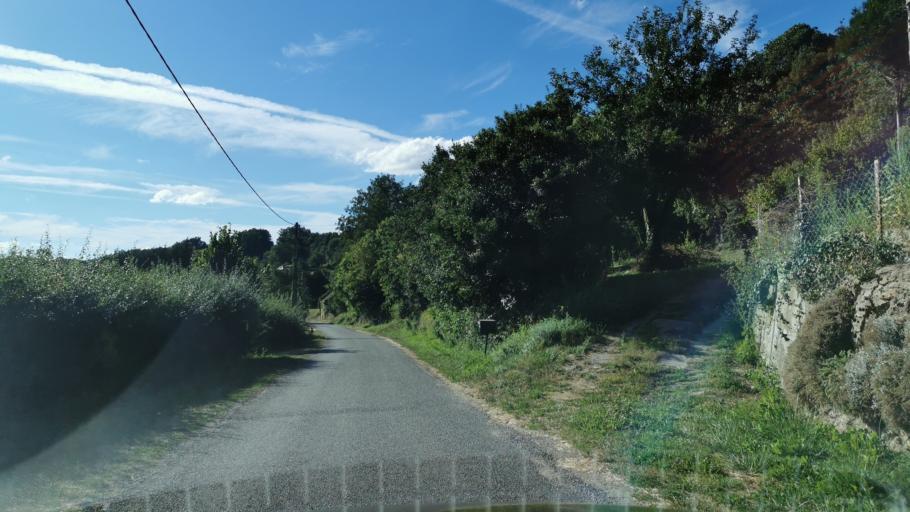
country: FR
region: Bourgogne
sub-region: Departement de Saone-et-Loire
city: Marmagne
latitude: 46.8736
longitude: 4.3413
